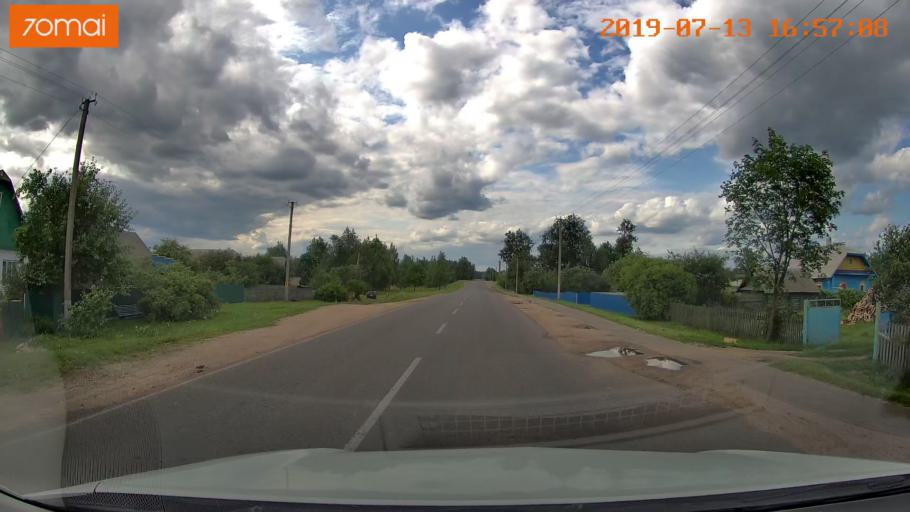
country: BY
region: Mogilev
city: Kirawsk
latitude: 53.2776
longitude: 29.4544
